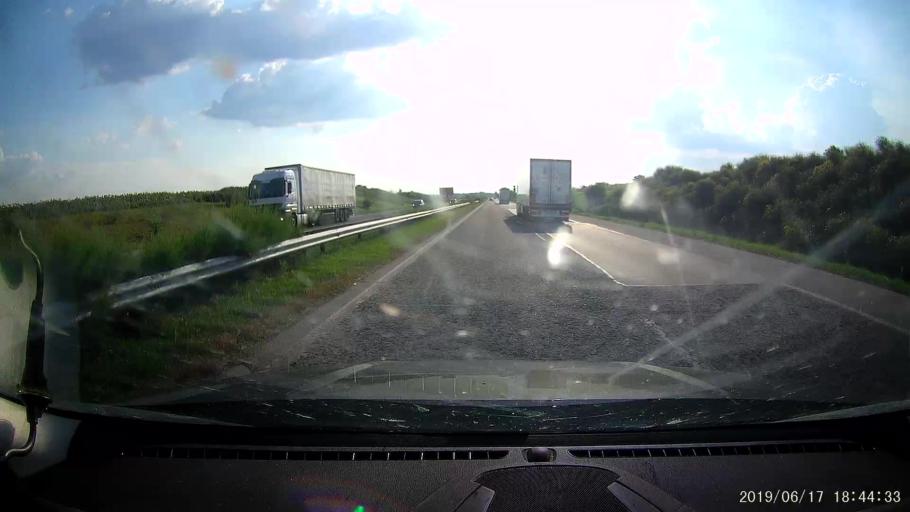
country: BG
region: Stara Zagora
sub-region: Obshtina Chirpan
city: Chirpan
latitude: 42.1930
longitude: 25.1781
